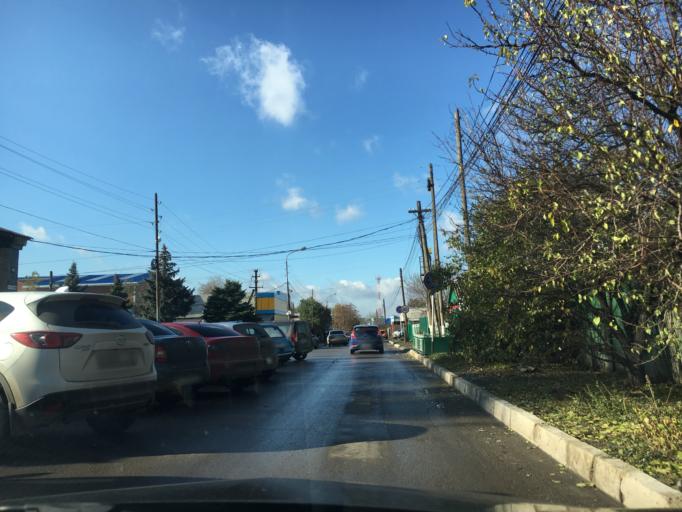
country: RU
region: Rostov
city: Matveyev Kurgan
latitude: 47.5659
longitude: 38.8658
